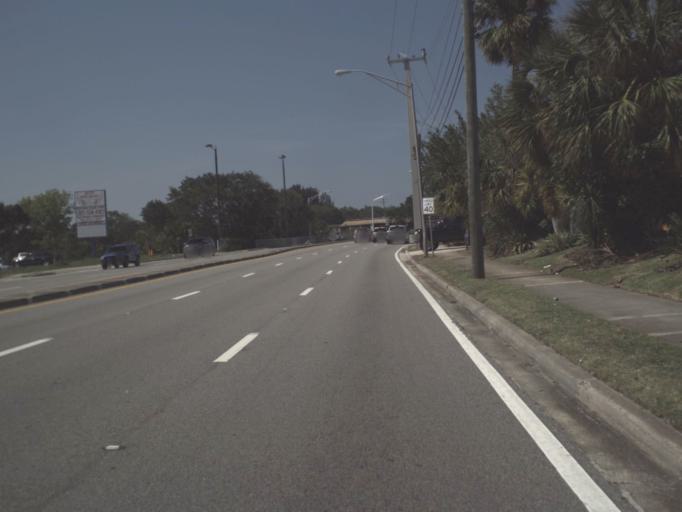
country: US
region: Florida
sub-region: Brevard County
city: Melbourne
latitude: 28.1223
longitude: -80.6309
